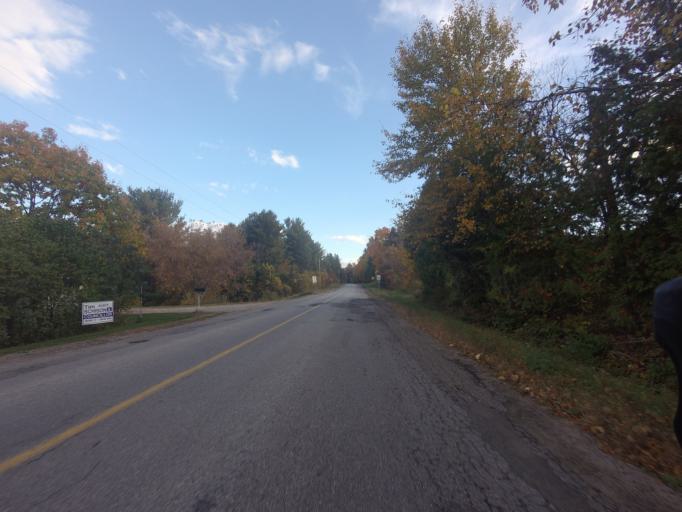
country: CA
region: Ontario
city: Pembroke
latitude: 45.5293
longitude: -77.0869
